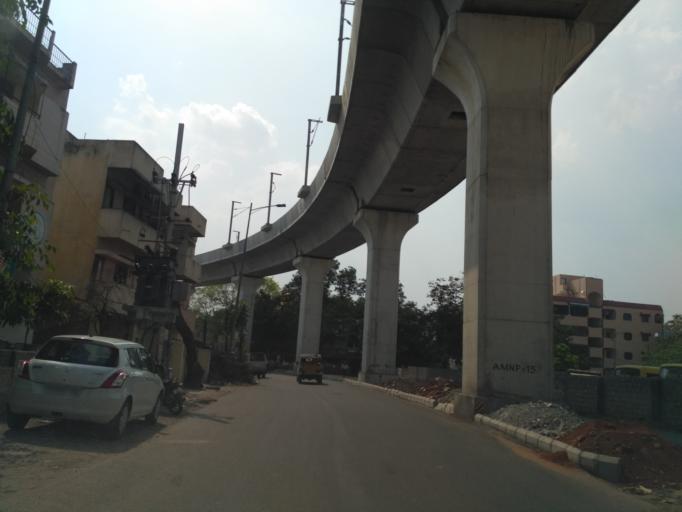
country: IN
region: Telangana
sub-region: Rangareddi
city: Kukatpalli
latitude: 17.4375
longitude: 78.4411
